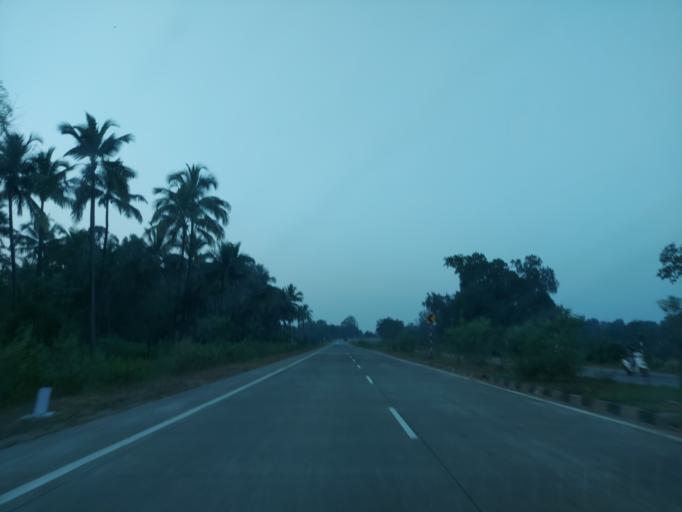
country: IN
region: Maharashtra
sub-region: Sindhudurg
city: Kudal
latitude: 16.0894
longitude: 73.7079
